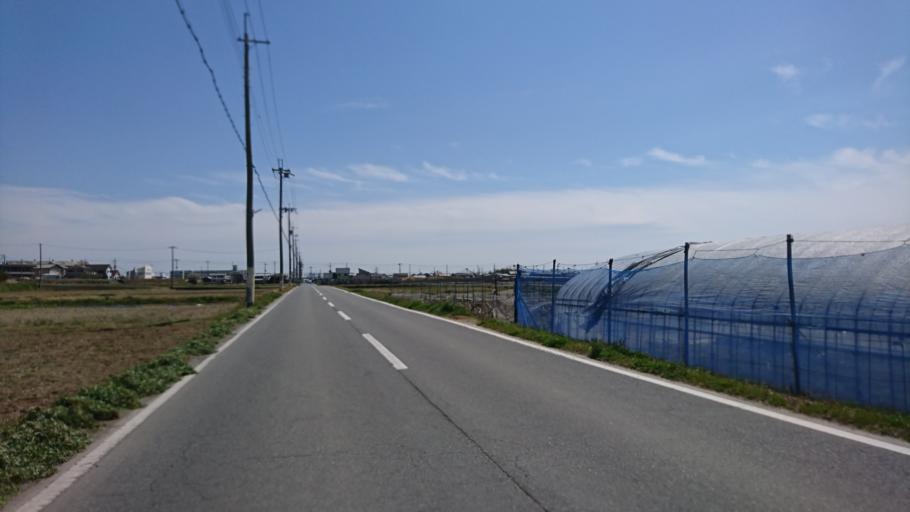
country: JP
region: Hyogo
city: Kakogawacho-honmachi
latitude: 34.7472
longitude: 134.8890
